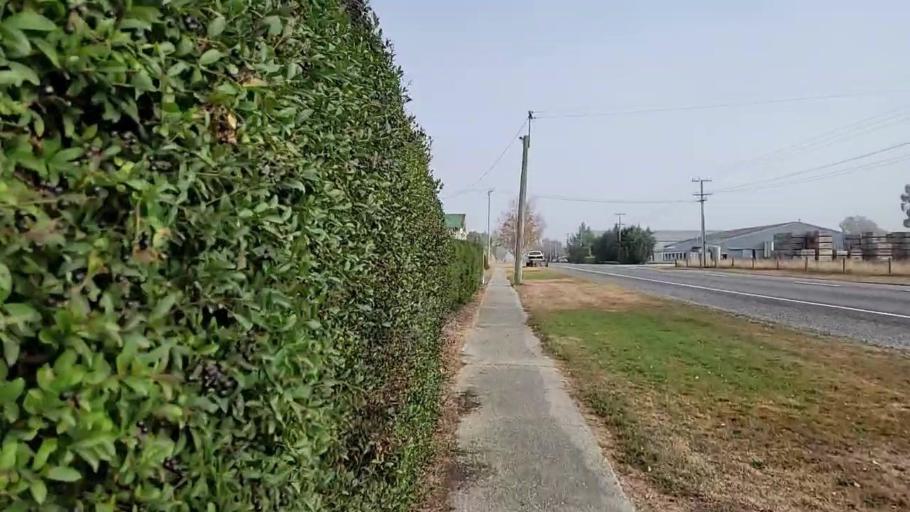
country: NZ
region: Southland
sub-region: Gore District
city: Gore
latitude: -45.6376
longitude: 169.3680
